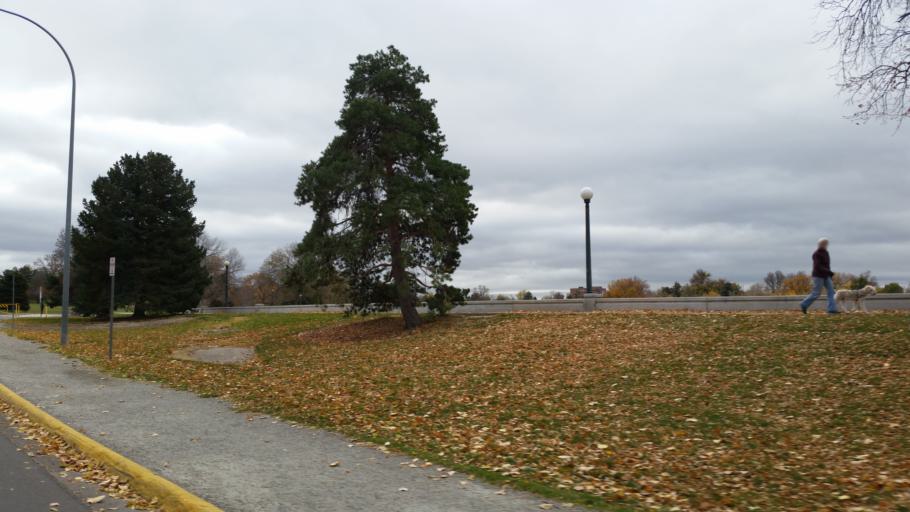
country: US
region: Colorado
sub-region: Denver County
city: Denver
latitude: 39.7477
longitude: -104.9494
